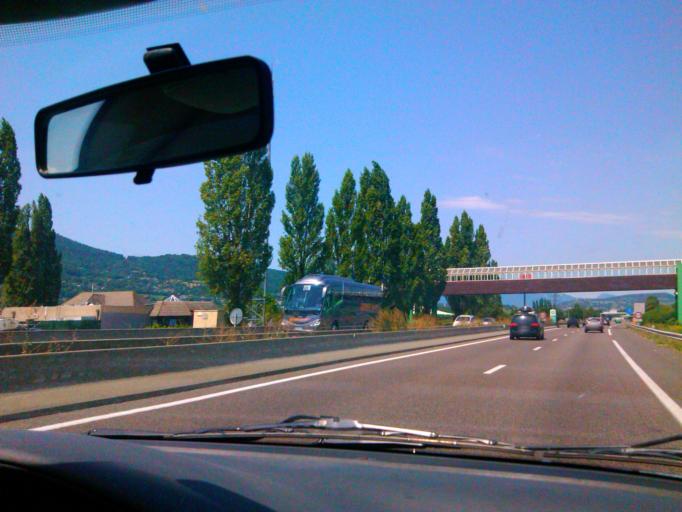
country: FR
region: Rhone-Alpes
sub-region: Departement de la Savoie
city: Saint-Baldoph
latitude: 45.5247
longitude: 5.9763
